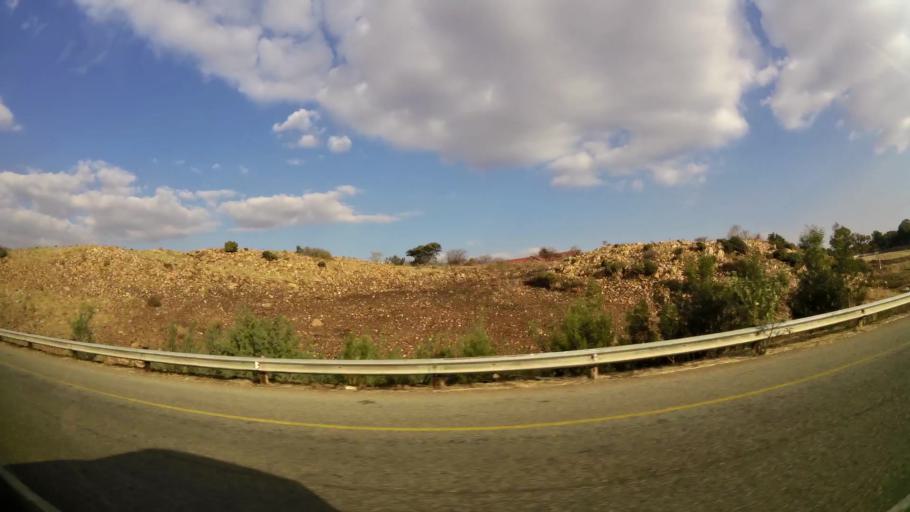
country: ZA
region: Gauteng
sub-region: West Rand District Municipality
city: Krugersdorp
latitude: -26.0849
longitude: 27.7419
